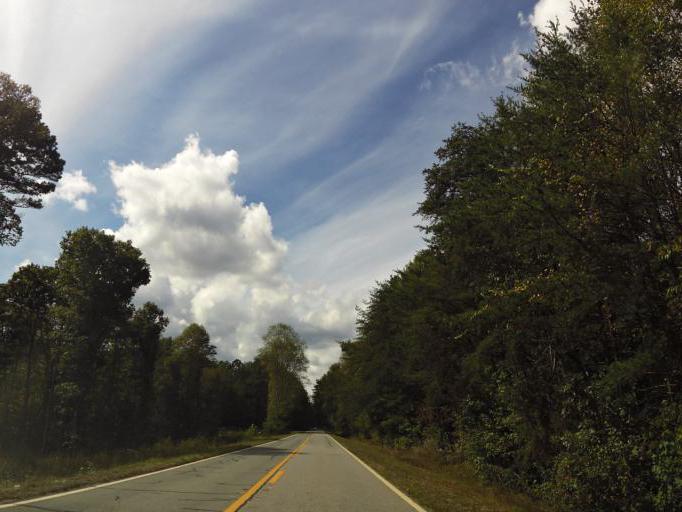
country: US
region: Georgia
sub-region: Dawson County
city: Dawsonville
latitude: 34.5236
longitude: -84.2577
